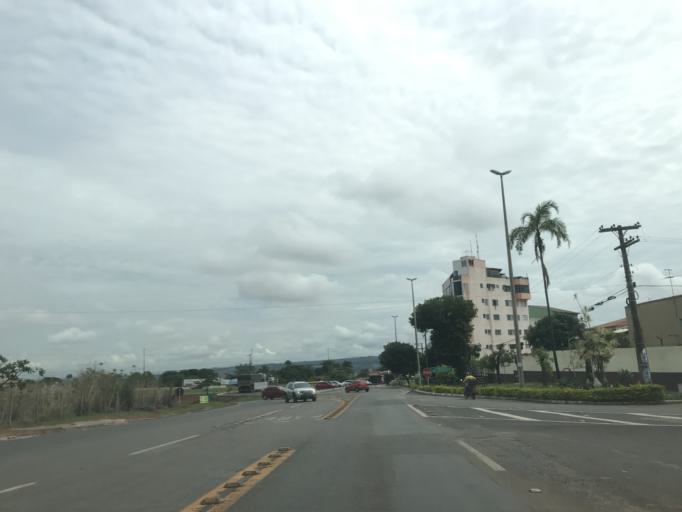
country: BR
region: Federal District
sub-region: Brasilia
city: Brasilia
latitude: -15.6834
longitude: -47.8372
